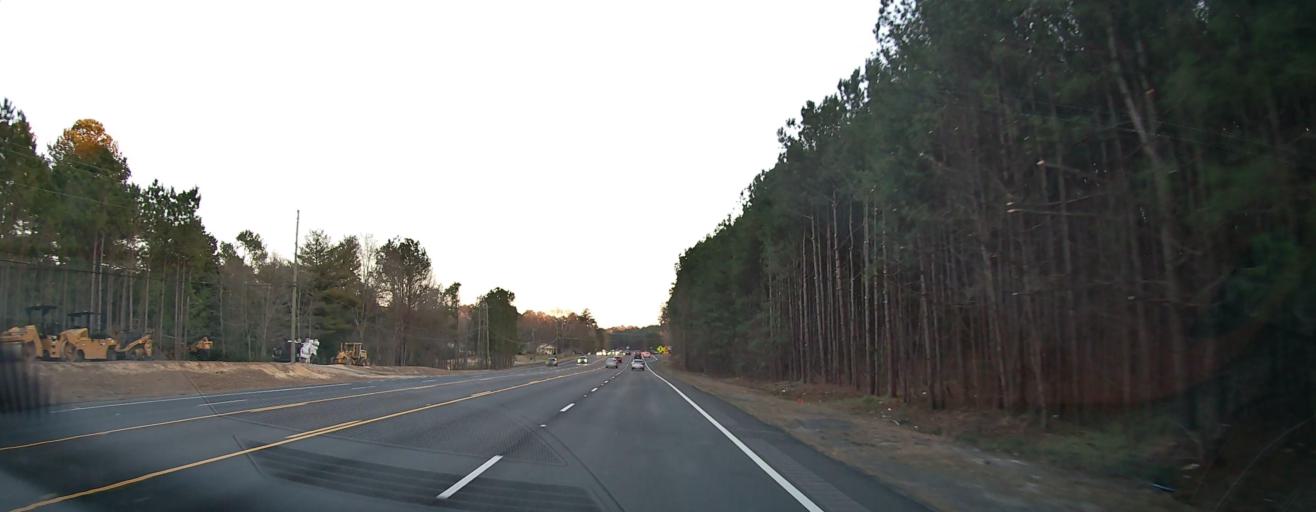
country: US
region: Georgia
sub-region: Fulton County
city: Union City
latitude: 33.5579
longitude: -84.5047
